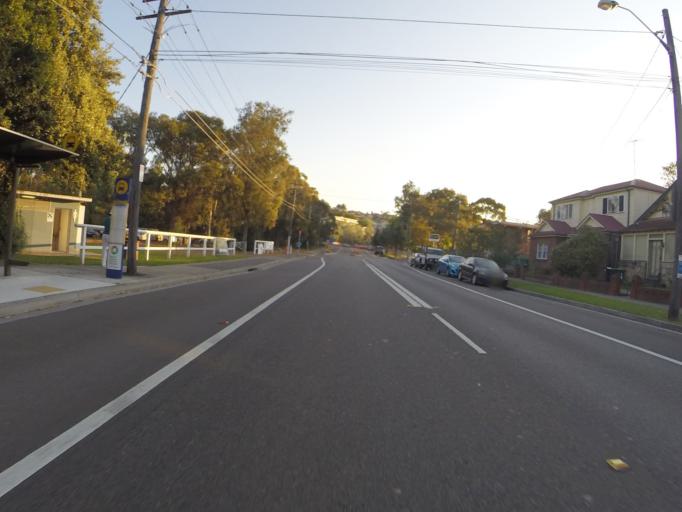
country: AU
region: New South Wales
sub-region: Rockdale
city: Bardwell Valley
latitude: -33.9210
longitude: 151.1439
